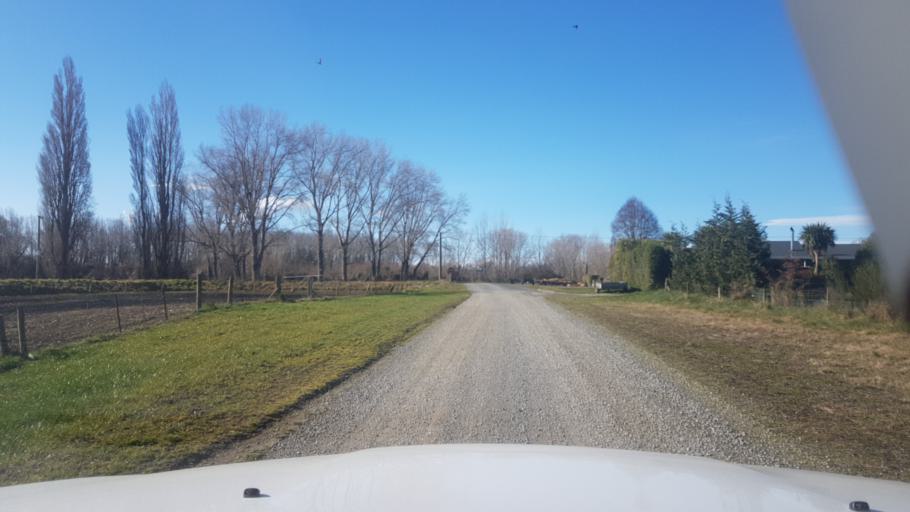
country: NZ
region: Canterbury
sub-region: Timaru District
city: Pleasant Point
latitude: -44.2487
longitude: 171.1167
